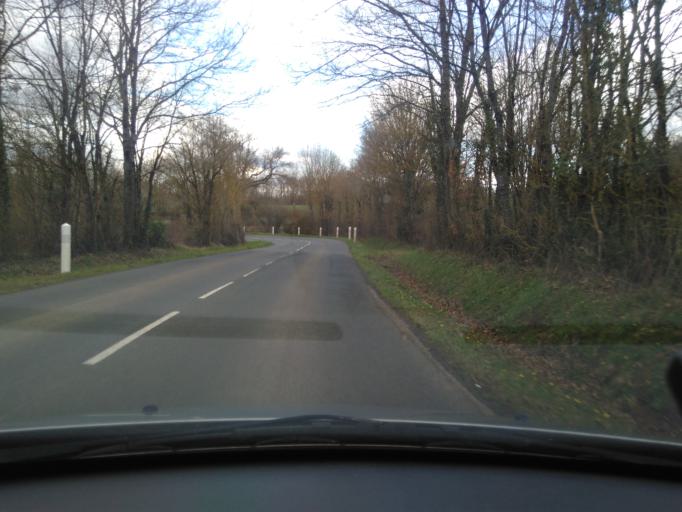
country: FR
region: Pays de la Loire
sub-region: Departement de la Vendee
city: Sainte-Cecile
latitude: 46.6908
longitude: -1.1096
